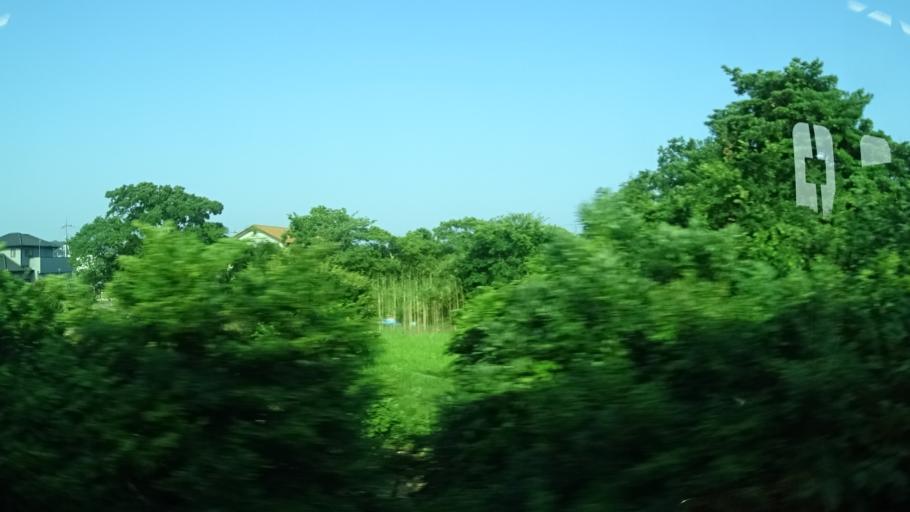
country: JP
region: Ibaraki
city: Kitaibaraki
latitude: 36.8308
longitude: 140.7763
